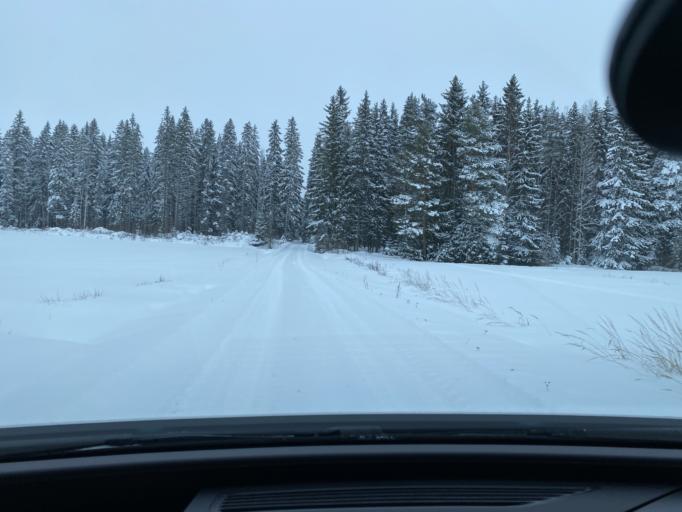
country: FI
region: Pirkanmaa
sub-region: Lounais-Pirkanmaa
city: Punkalaidun
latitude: 61.1306
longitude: 23.0918
